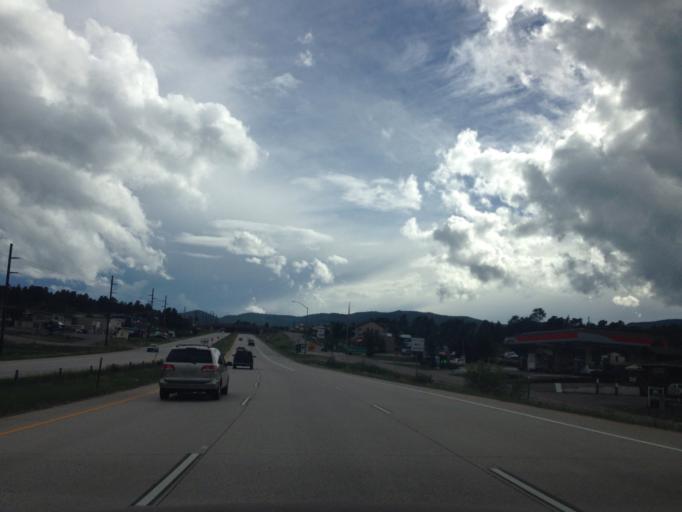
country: US
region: Colorado
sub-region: Jefferson County
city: Evergreen
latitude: 39.5420
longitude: -105.2959
